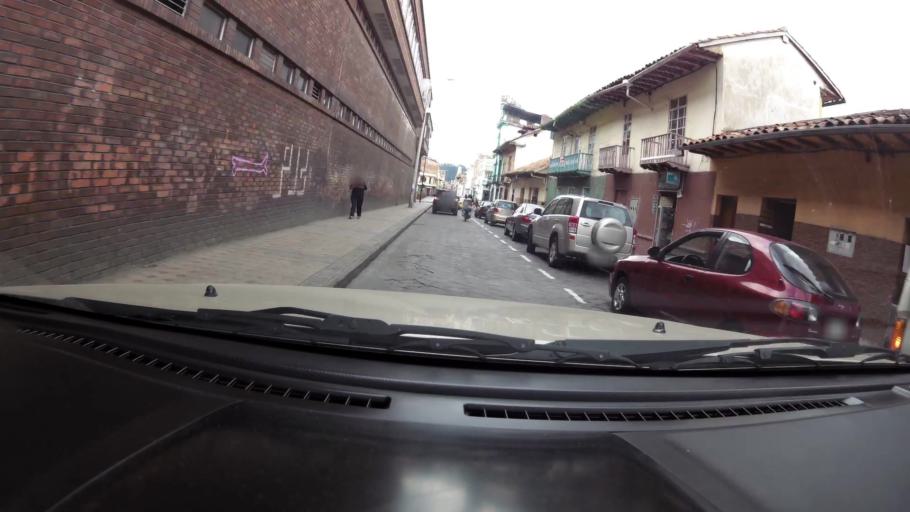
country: EC
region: Azuay
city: Cuenca
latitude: -2.8916
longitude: -79.0059
